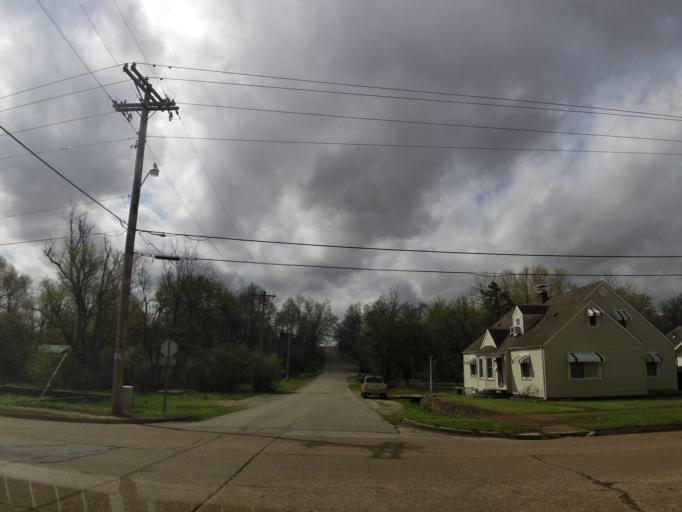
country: US
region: Missouri
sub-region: Butler County
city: Poplar Bluff
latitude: 36.7539
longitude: -90.4003
